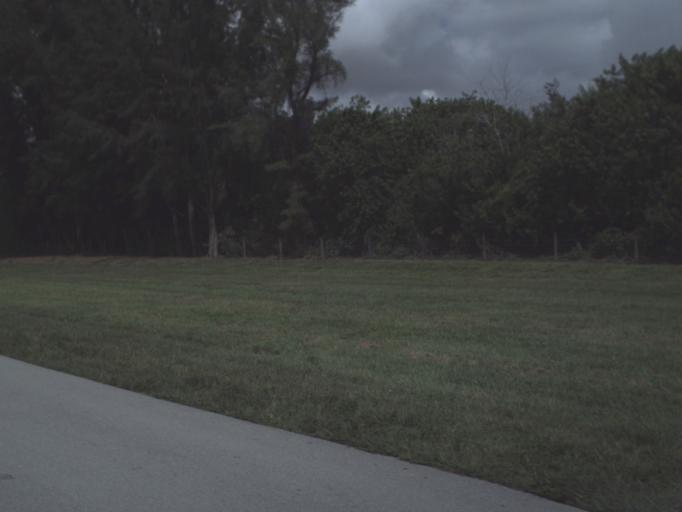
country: US
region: Florida
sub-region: Palm Beach County
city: Kings Point
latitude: 26.4303
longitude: -80.1723
